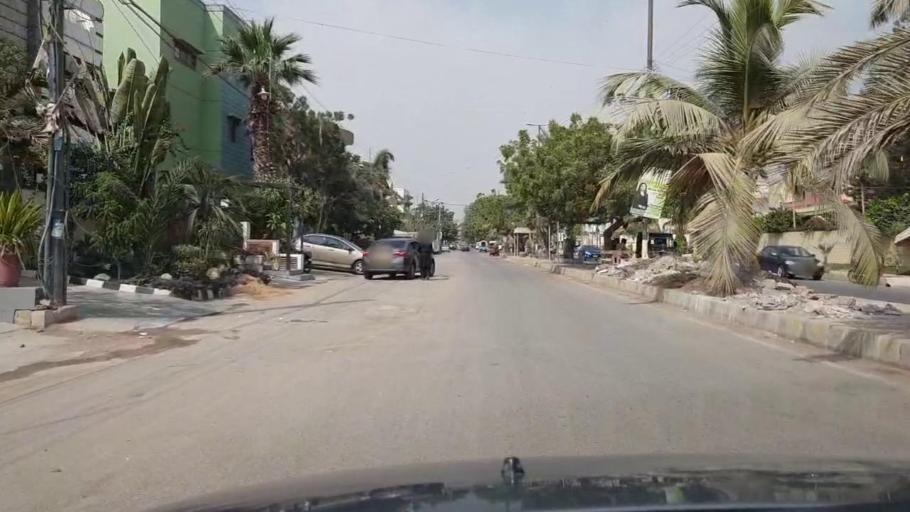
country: PK
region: Sindh
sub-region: Karachi District
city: Karachi
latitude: 24.8740
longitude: 67.0867
